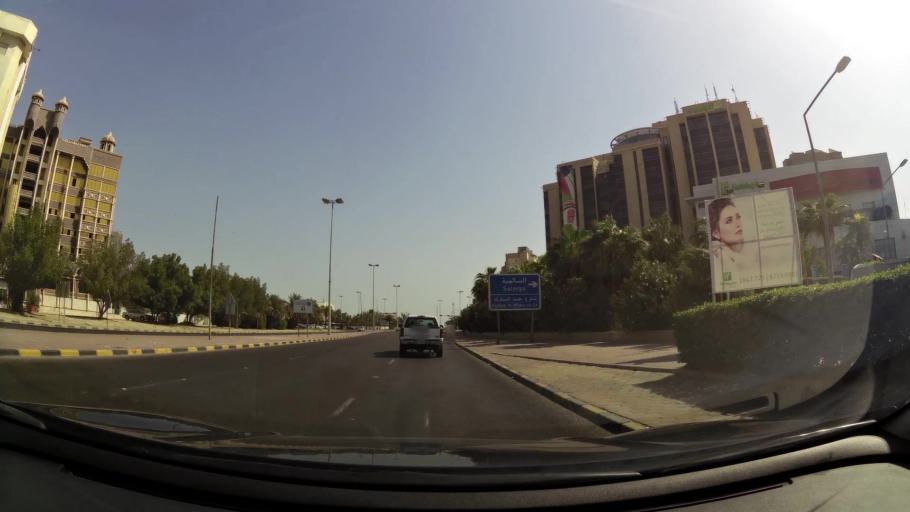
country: KW
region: Muhafazat Hawalli
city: As Salimiyah
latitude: 29.3474
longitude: 48.0935
